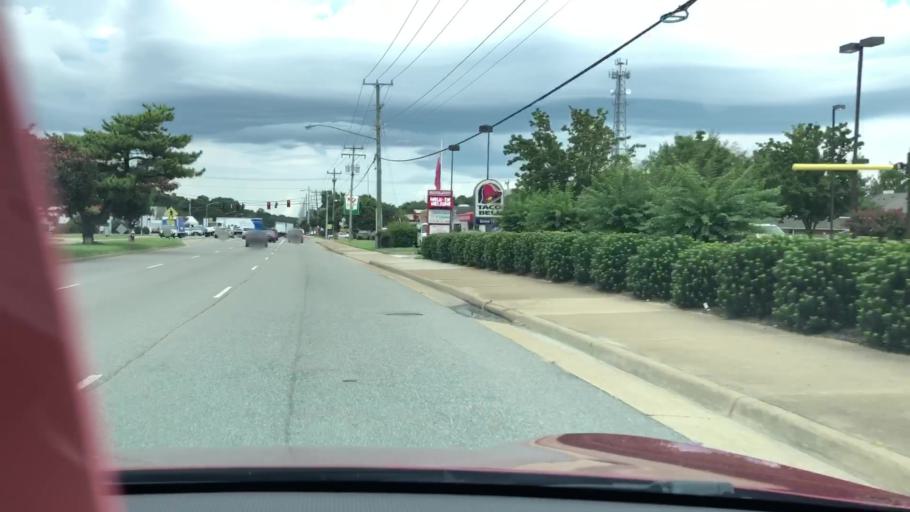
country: US
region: Virginia
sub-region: City of Virginia Beach
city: Virginia Beach
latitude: 36.8775
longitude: -76.0408
